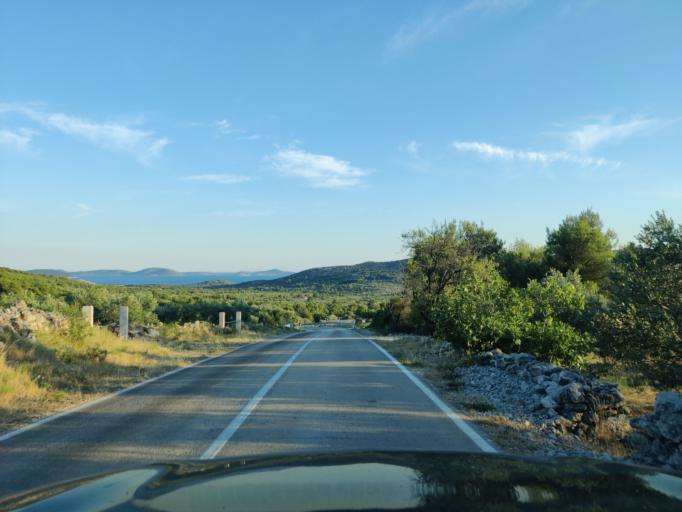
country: HR
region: Sibensko-Kniniska
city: Tribunj
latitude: 43.7868
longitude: 15.7265
